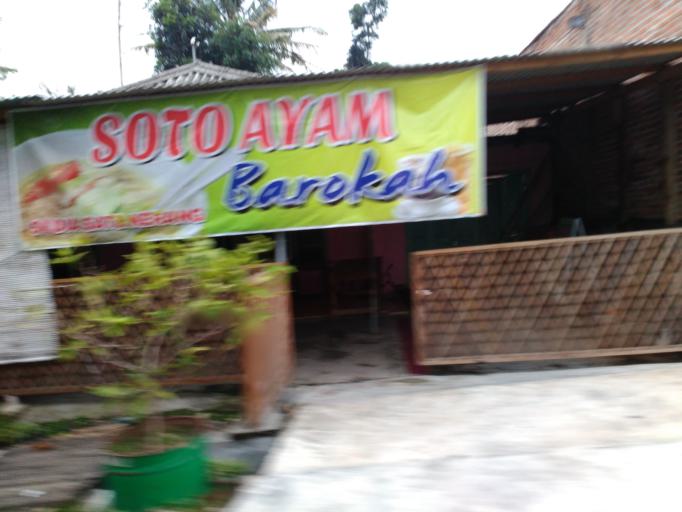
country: ID
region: Central Java
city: Boyolali
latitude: -7.5231
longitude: 110.5952
